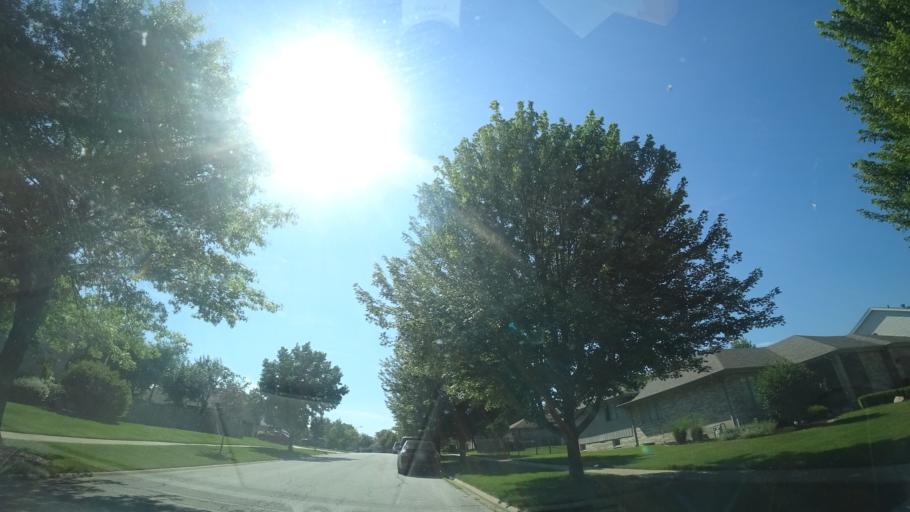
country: US
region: Illinois
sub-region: Will County
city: Mokena
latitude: 41.5697
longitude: -87.9026
